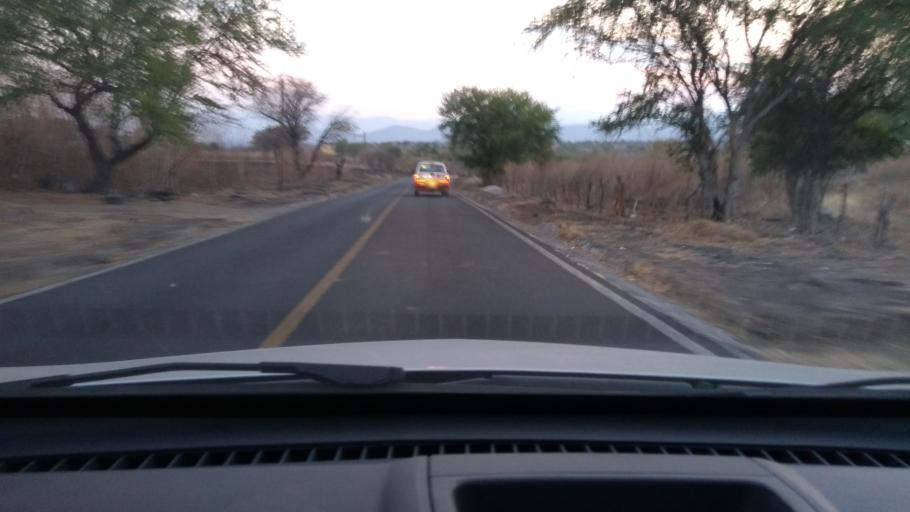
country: MX
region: Morelos
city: Coatetelco
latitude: 18.7229
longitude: -99.3031
